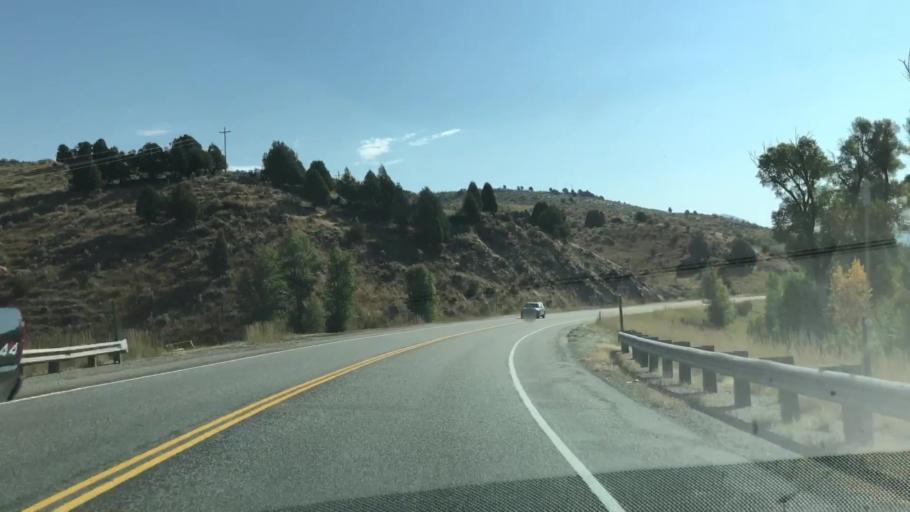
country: US
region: Idaho
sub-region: Teton County
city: Victor
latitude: 43.4511
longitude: -111.3962
